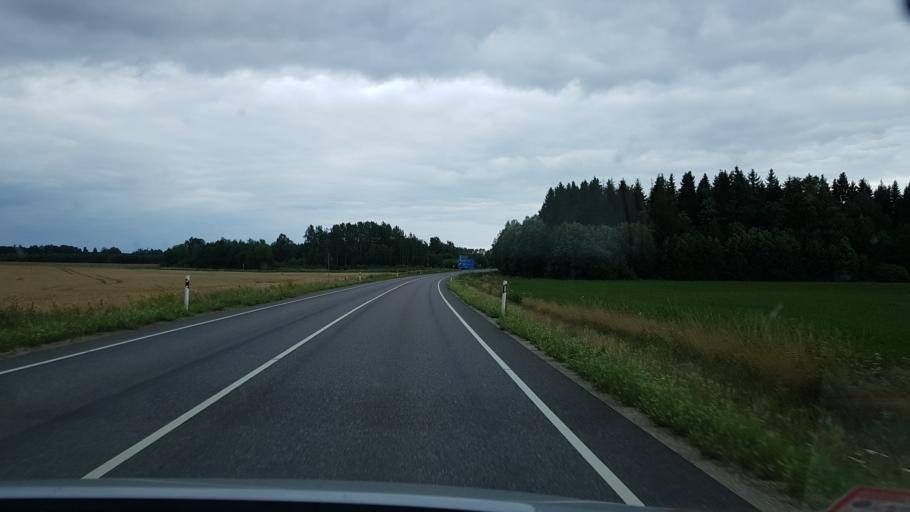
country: EE
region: Tartu
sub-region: Tartu linn
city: Tartu
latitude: 58.4070
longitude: 26.8940
